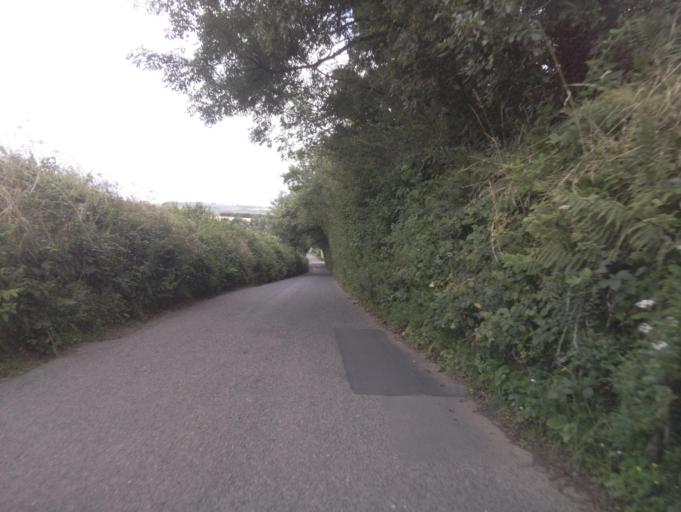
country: GB
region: England
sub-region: Devon
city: South Brent
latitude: 50.4001
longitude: -3.8313
